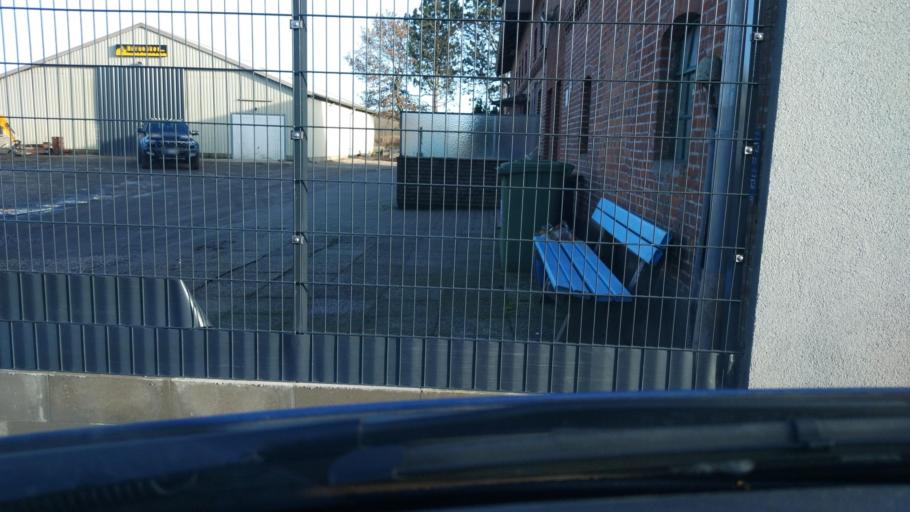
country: DE
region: Schleswig-Holstein
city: Jerrishoe
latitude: 54.6741
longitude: 9.3738
